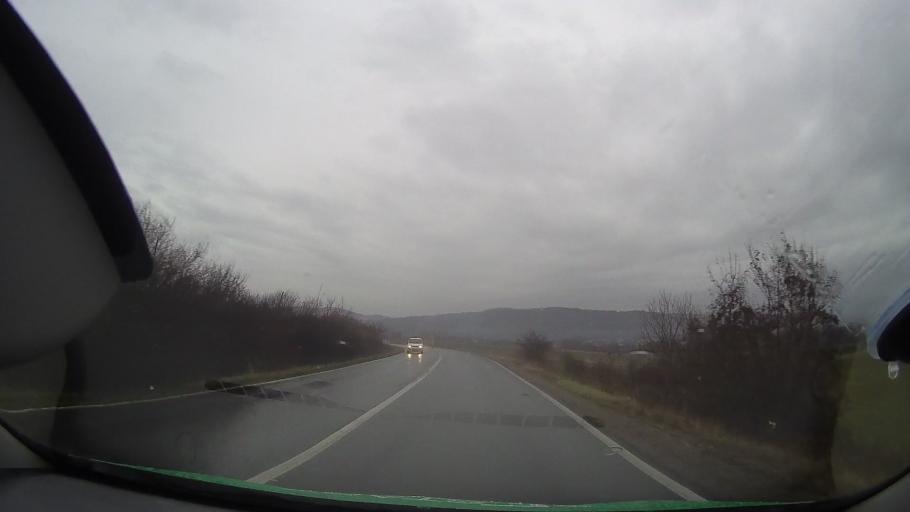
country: RO
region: Bihor
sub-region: Comuna Rabagani
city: Rabagani
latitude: 46.7413
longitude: 22.2286
